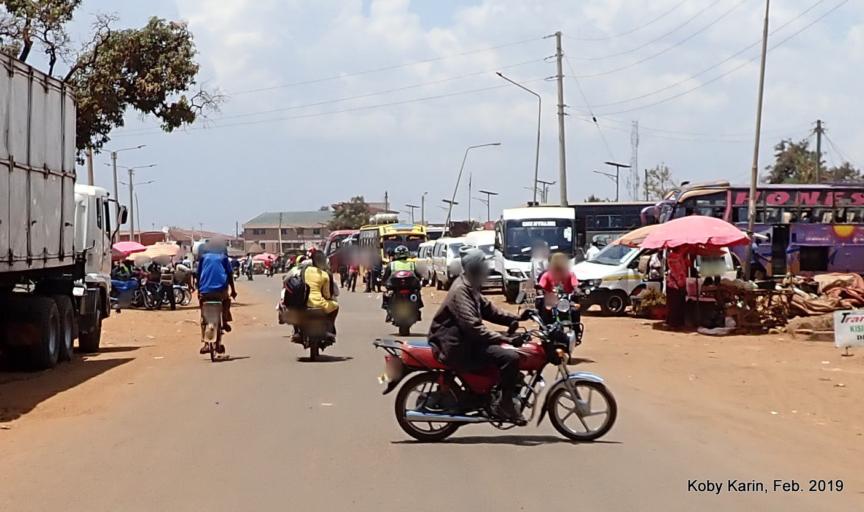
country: KE
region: Busia
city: Busia
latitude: 0.4612
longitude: 34.1099
